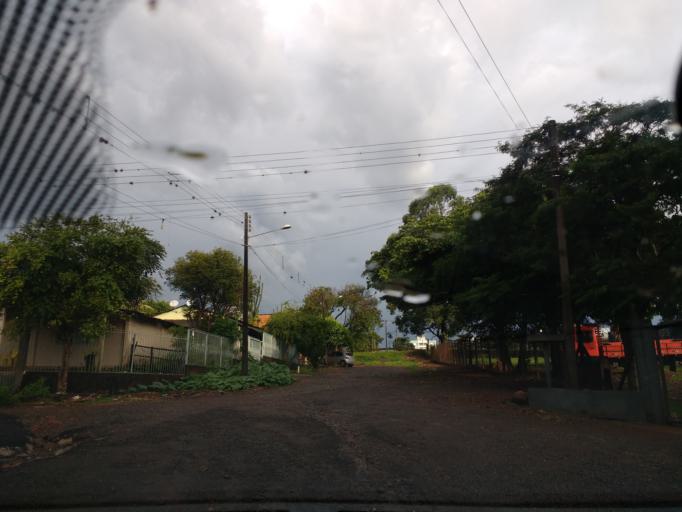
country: BR
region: Parana
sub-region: Londrina
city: Londrina
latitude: -23.2920
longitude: -51.1461
